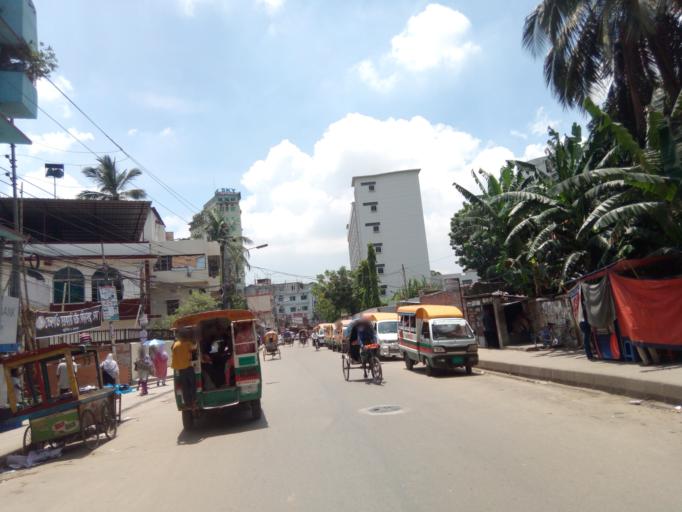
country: BD
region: Dhaka
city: Azimpur
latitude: 23.7575
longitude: 90.3920
